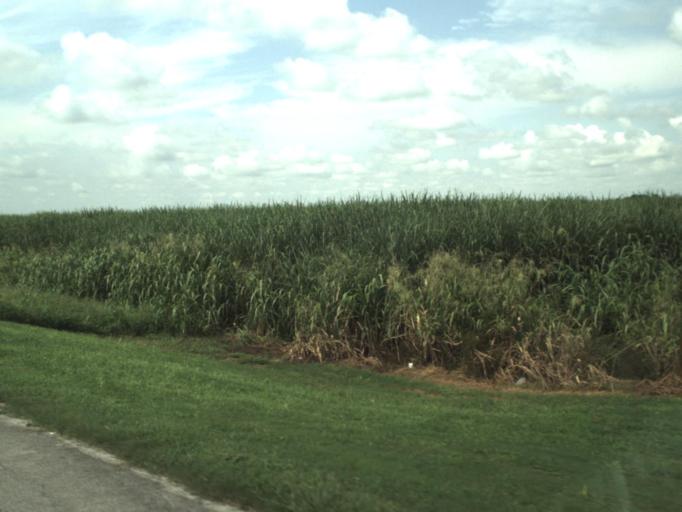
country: US
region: Florida
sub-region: Palm Beach County
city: Belle Glade Camp
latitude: 26.6748
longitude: -80.6867
